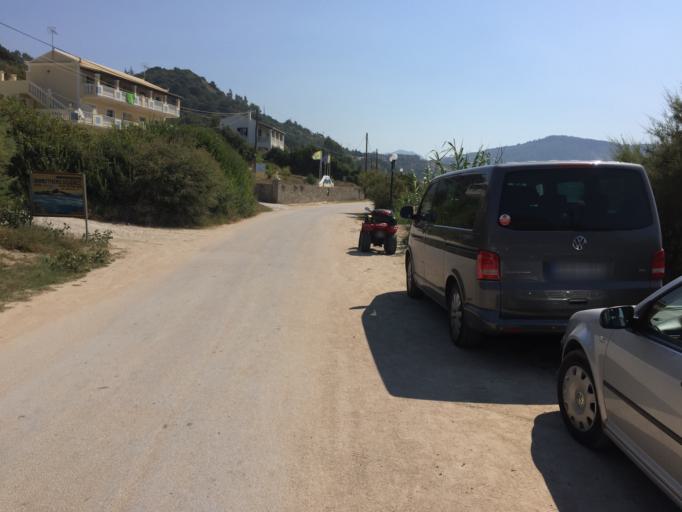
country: GR
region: Ionian Islands
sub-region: Nomos Kerkyras
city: Agios Georgis
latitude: 39.7225
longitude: 19.6664
